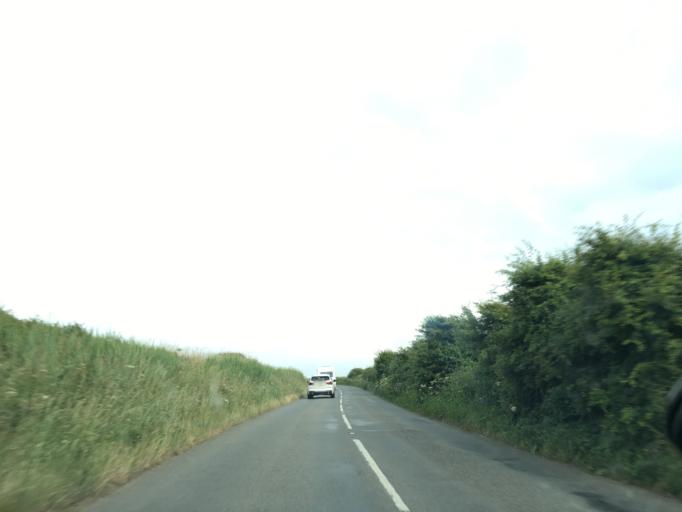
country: GB
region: England
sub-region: Isle of Wight
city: Shalfleet
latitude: 50.6442
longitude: -1.4380
